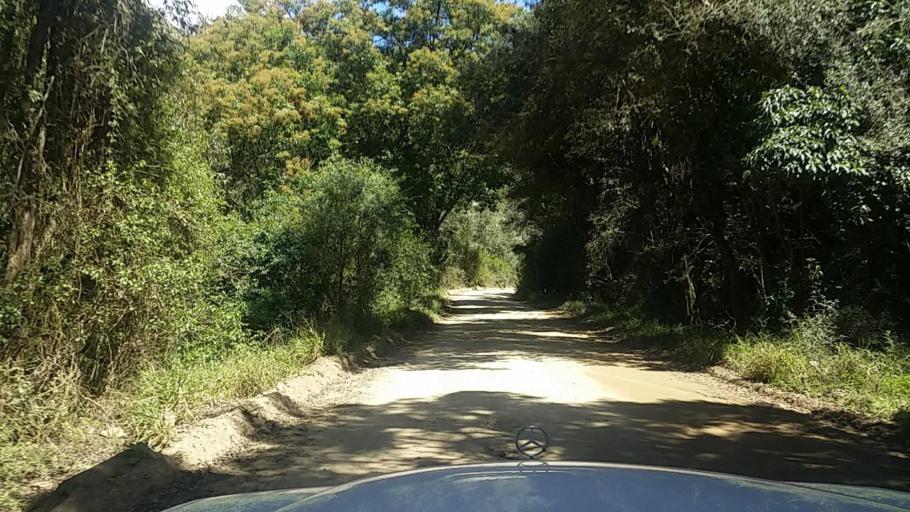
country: ZA
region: Western Cape
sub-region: Eden District Municipality
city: Knysna
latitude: -33.8604
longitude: 23.1748
